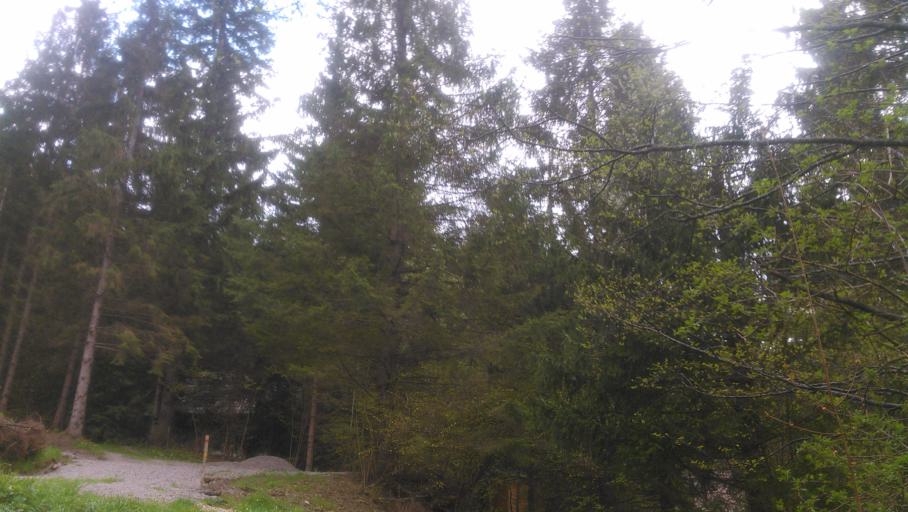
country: SK
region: Banskobystricky
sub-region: Okres Banska Bystrica
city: Brezno
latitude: 48.8712
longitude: 19.5689
